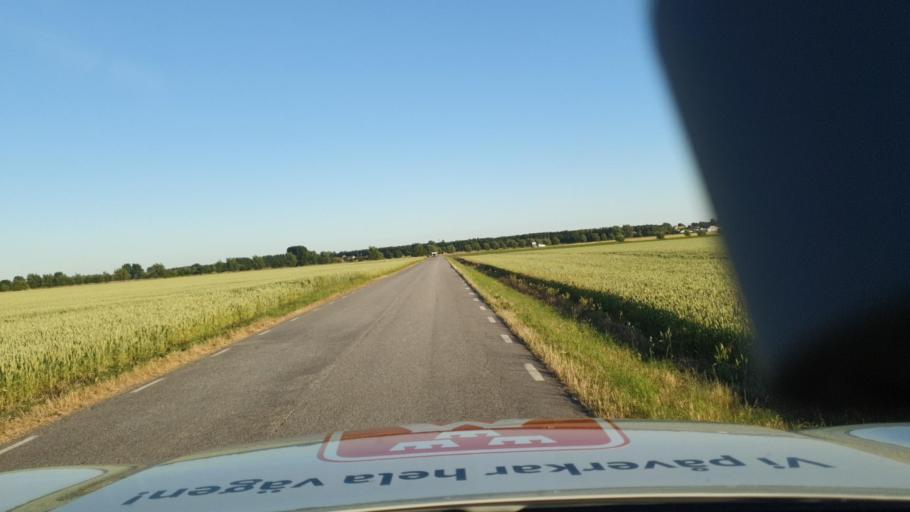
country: SE
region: Skane
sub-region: Lomma Kommun
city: Lomma
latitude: 55.7058
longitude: 13.0597
